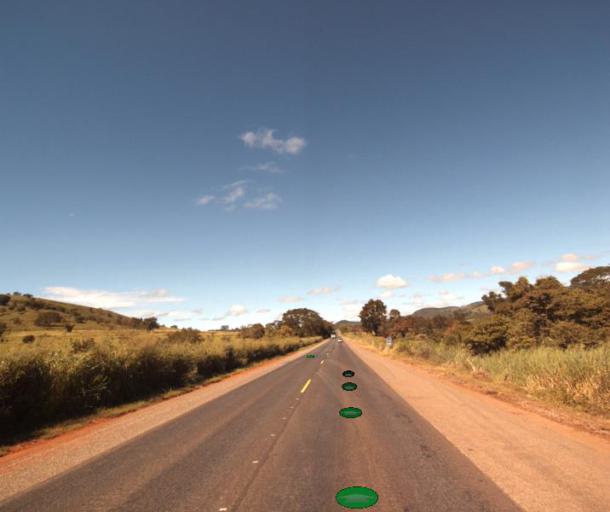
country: BR
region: Goias
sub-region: Ceres
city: Ceres
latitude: -15.2133
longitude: -49.5486
